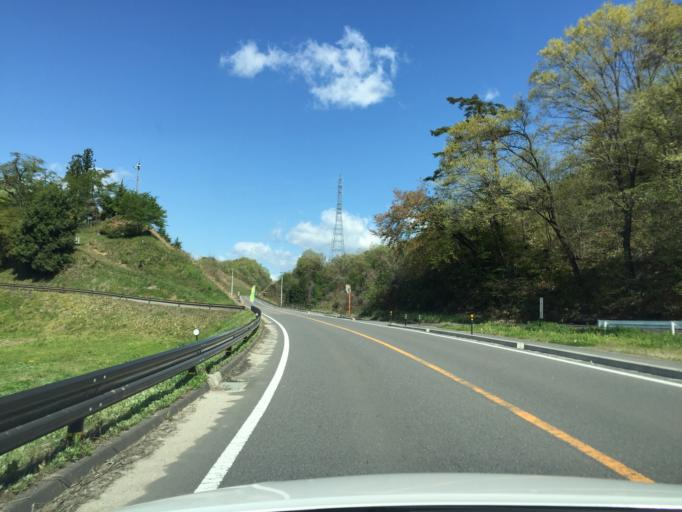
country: JP
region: Fukushima
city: Funehikimachi-funehiki
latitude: 37.5434
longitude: 140.5354
